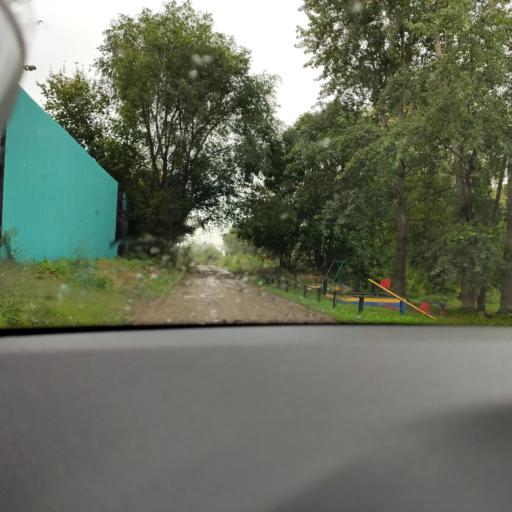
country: RU
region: Samara
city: Samara
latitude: 53.1722
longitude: 50.1583
